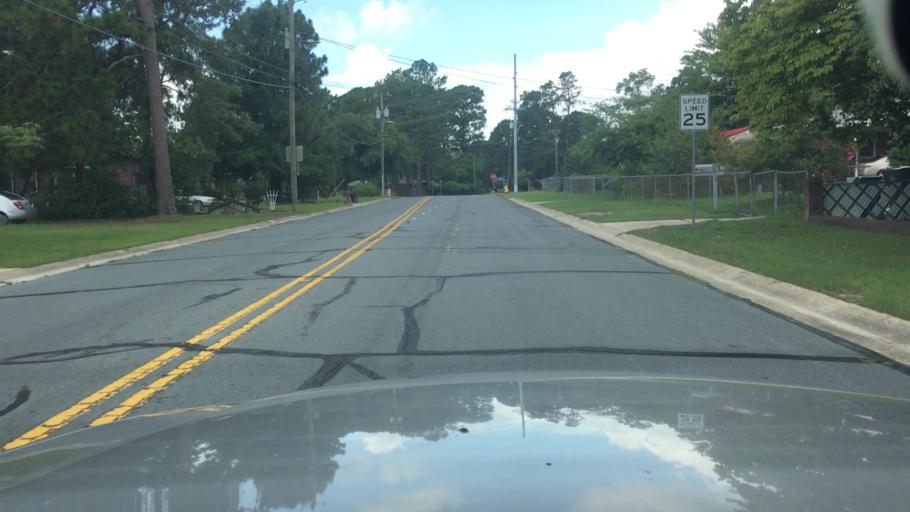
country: US
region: North Carolina
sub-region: Cumberland County
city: Hope Mills
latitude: 35.0209
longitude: -78.9388
